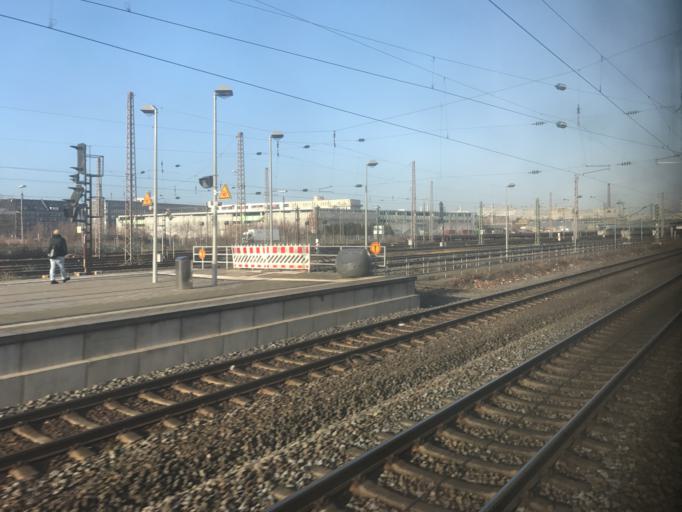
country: DE
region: North Rhine-Westphalia
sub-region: Regierungsbezirk Dusseldorf
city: Dusseldorf
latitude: 51.2487
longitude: 6.7943
